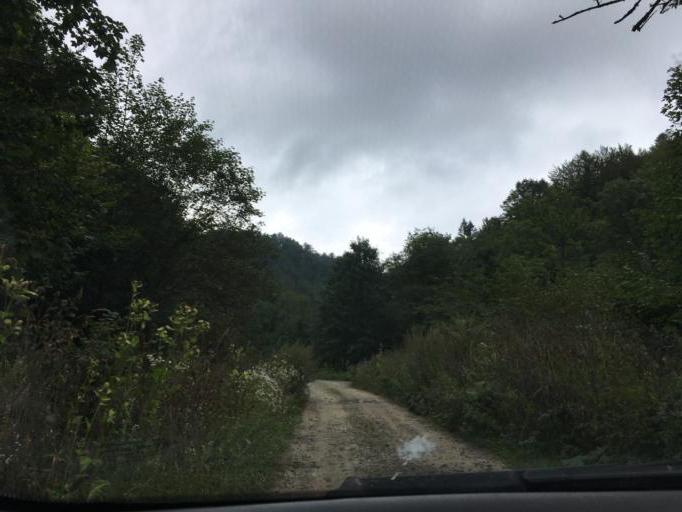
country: PL
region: Subcarpathian Voivodeship
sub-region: Powiat bieszczadzki
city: Lutowiska
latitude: 49.1826
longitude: 22.6168
